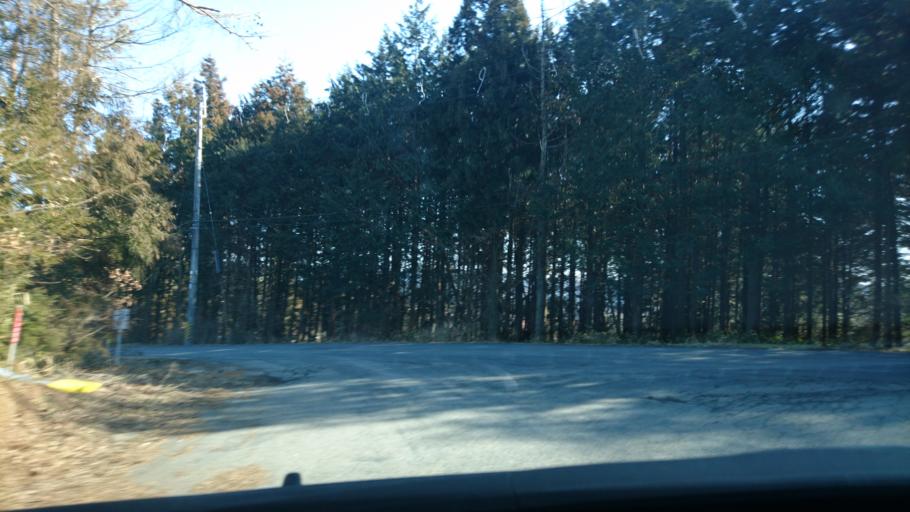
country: JP
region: Iwate
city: Ichinoseki
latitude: 38.8477
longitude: 141.2362
